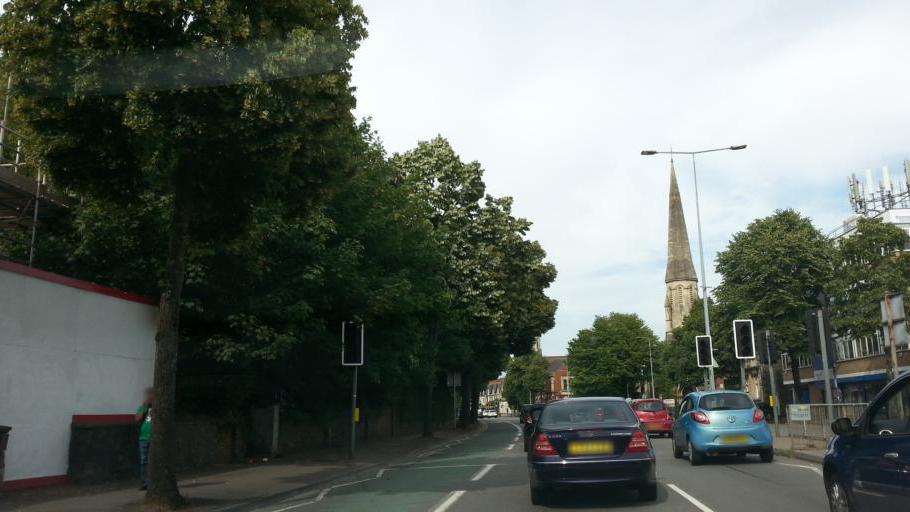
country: GB
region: Wales
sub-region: Cardiff
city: Cardiff
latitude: 51.4861
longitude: -3.1619
